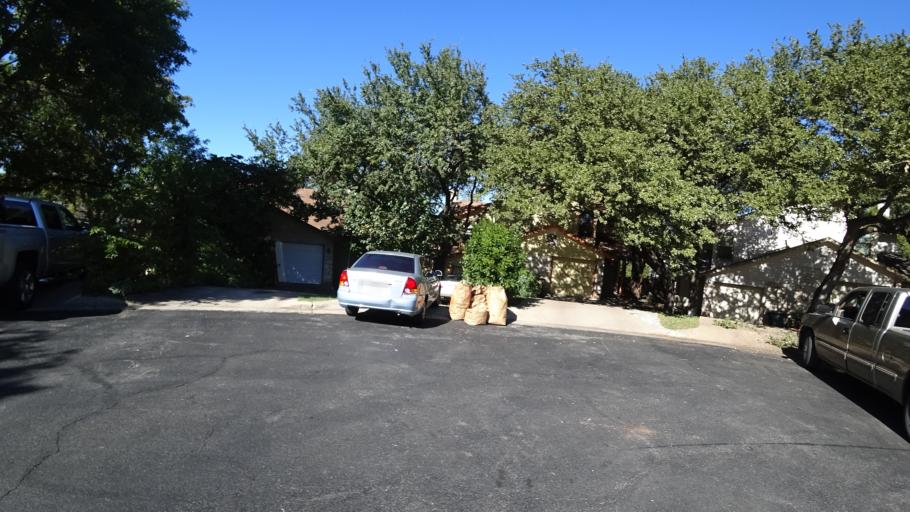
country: US
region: Texas
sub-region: Travis County
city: Rollingwood
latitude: 30.2386
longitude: -97.7818
